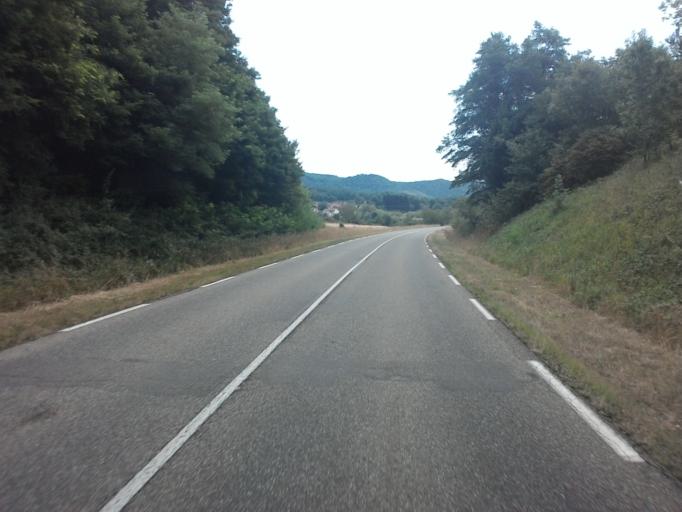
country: FR
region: Franche-Comte
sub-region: Departement du Jura
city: Saint-Amour
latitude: 46.4384
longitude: 5.3528
